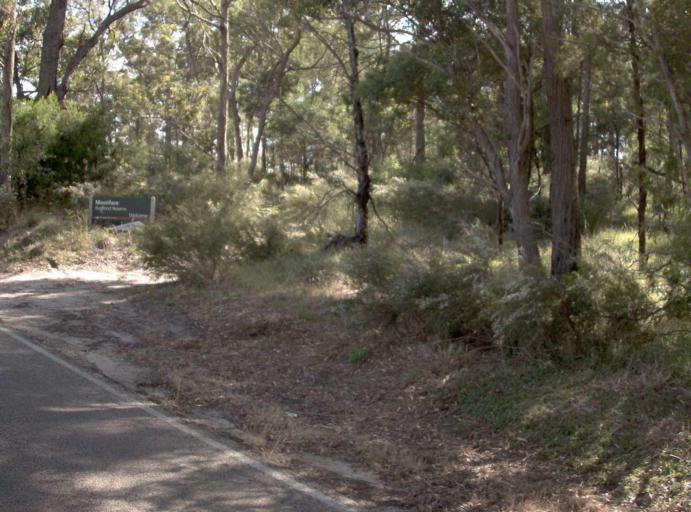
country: AU
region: Victoria
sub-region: East Gippsland
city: Lakes Entrance
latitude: -37.7451
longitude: 147.8138
